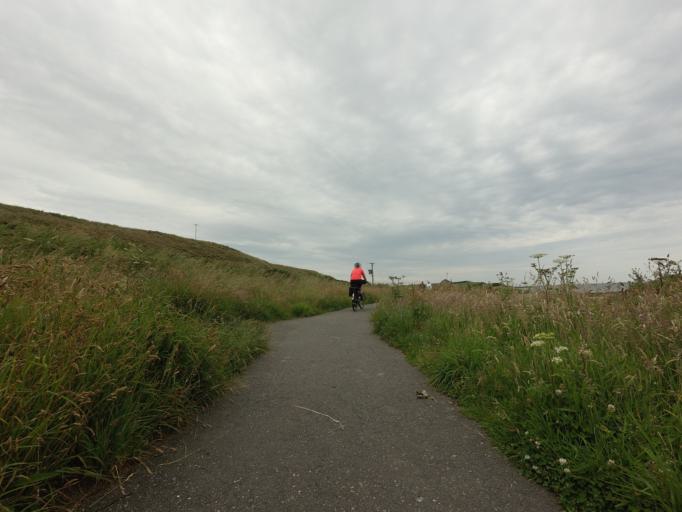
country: GB
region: Scotland
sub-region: Aberdeenshire
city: Whitehills
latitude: 57.6717
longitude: -2.5592
